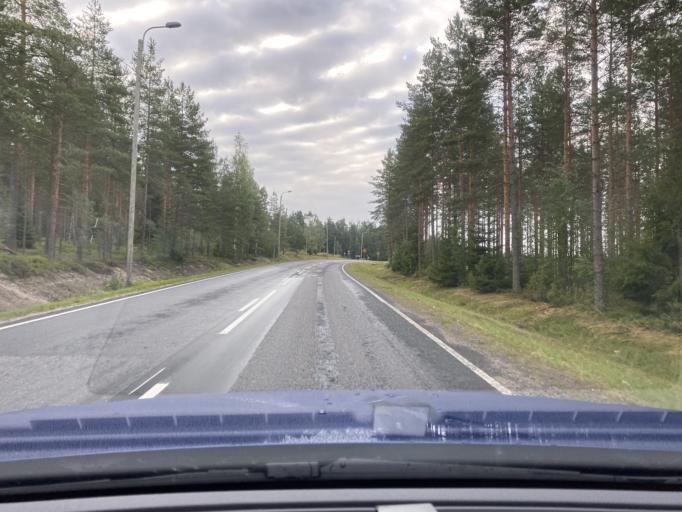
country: FI
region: Southern Ostrobothnia
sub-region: Seinaejoki
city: Jurva
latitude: 62.6775
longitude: 21.9794
